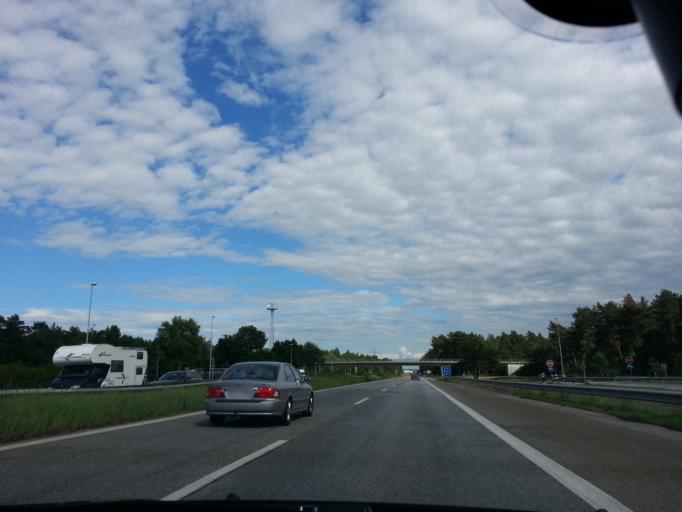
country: DE
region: Schleswig-Holstein
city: Gudow
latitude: 53.5195
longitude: 10.8094
